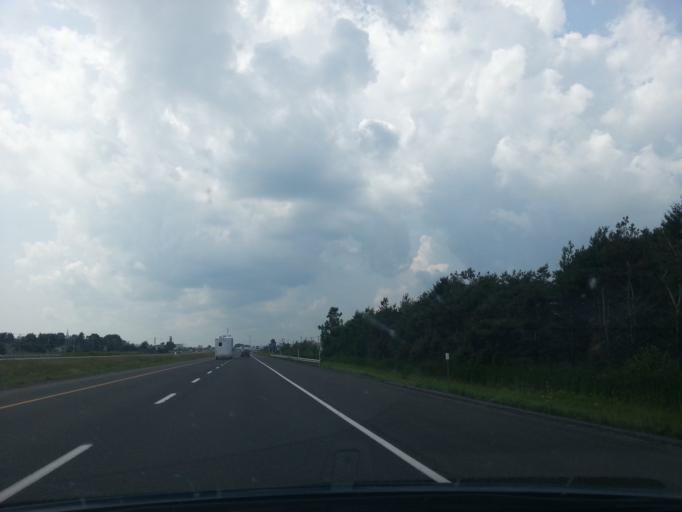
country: CA
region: Quebec
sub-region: Chaudiere-Appalaches
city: Saint-Antoine-de-Tilly
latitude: 46.6249
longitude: -71.4948
